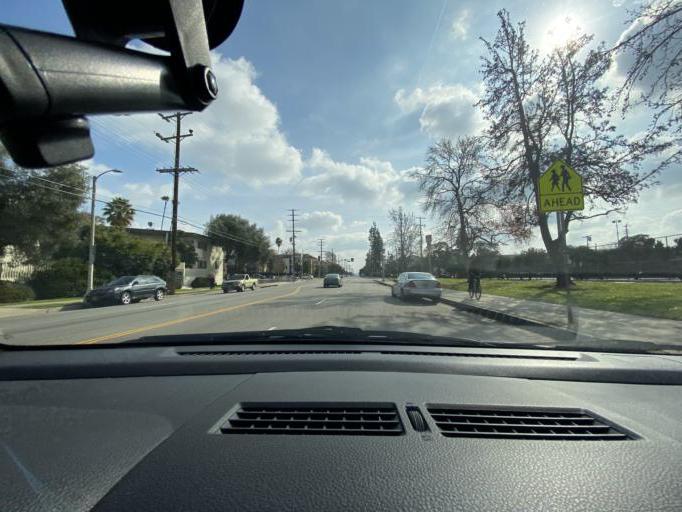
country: US
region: California
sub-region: Los Angeles County
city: Culver City
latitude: 34.0189
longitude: -118.4258
